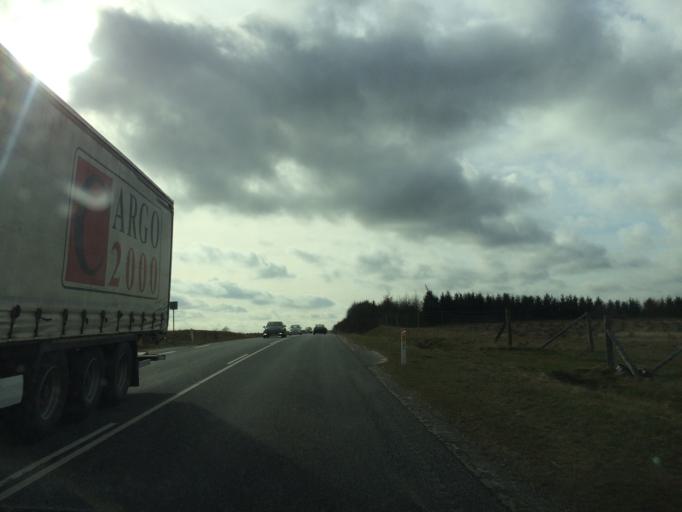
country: DK
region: Central Jutland
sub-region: Randers Kommune
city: Assentoft
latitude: 56.4422
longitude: 10.2154
